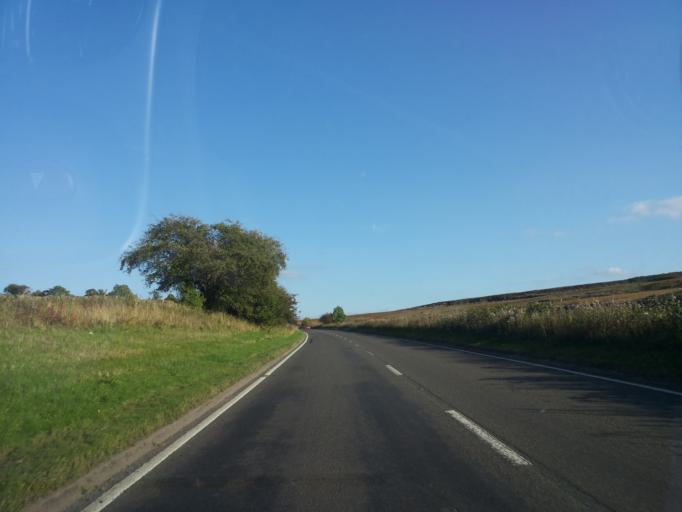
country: GB
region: England
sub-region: Derbyshire
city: Matlock
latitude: 53.2398
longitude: -1.5677
